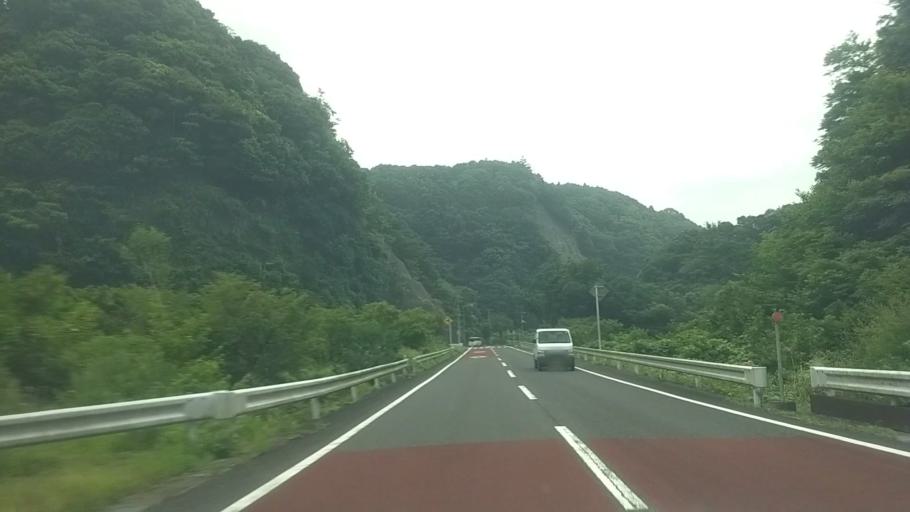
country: JP
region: Chiba
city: Kawaguchi
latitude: 35.2335
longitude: 140.1607
